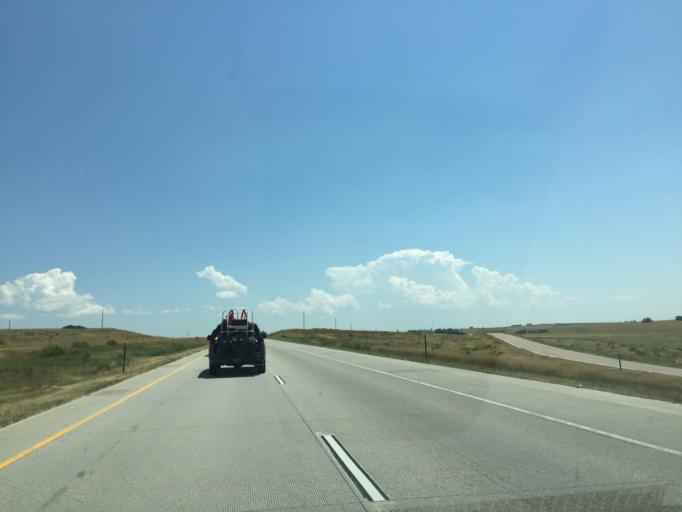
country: US
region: Colorado
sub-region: Lincoln County
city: Limon
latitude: 39.4893
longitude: -103.9573
